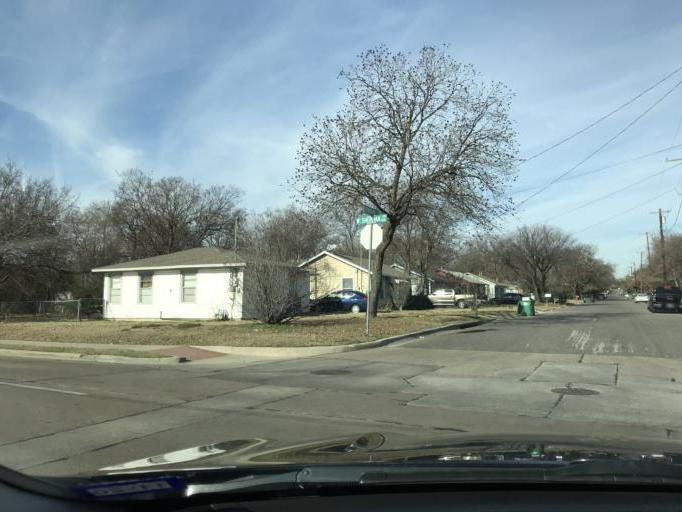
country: US
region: Texas
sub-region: Denton County
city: Denton
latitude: 33.2322
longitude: -97.1358
